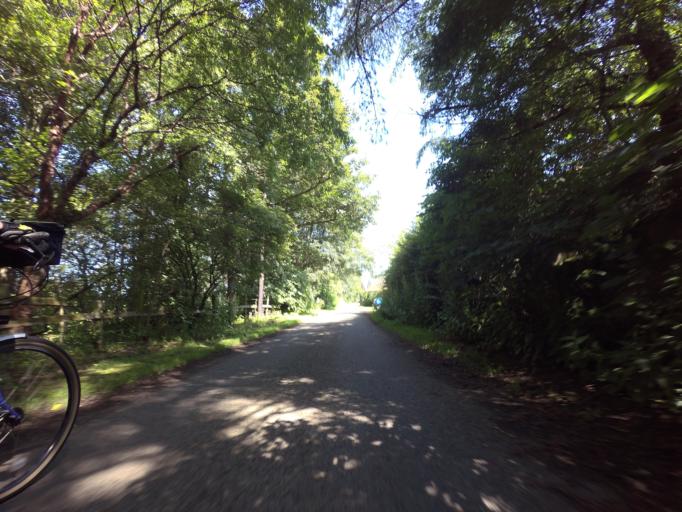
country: GB
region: Scotland
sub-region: Aberdeenshire
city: Banff
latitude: 57.6068
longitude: -2.5127
